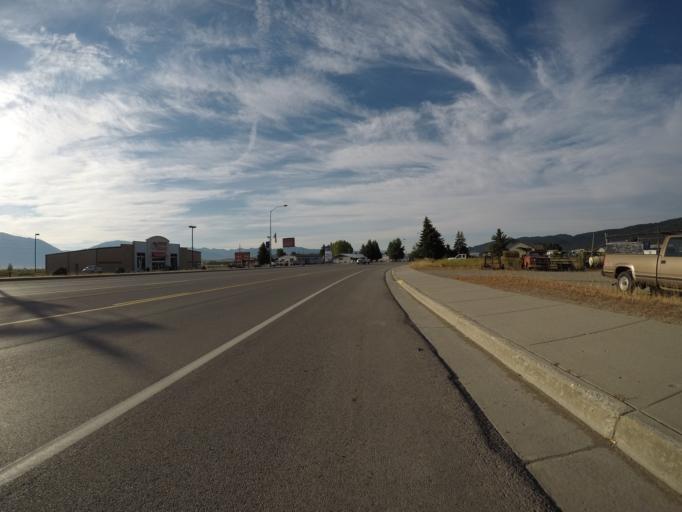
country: US
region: Wyoming
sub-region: Lincoln County
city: Afton
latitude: 42.9242
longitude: -111.0029
